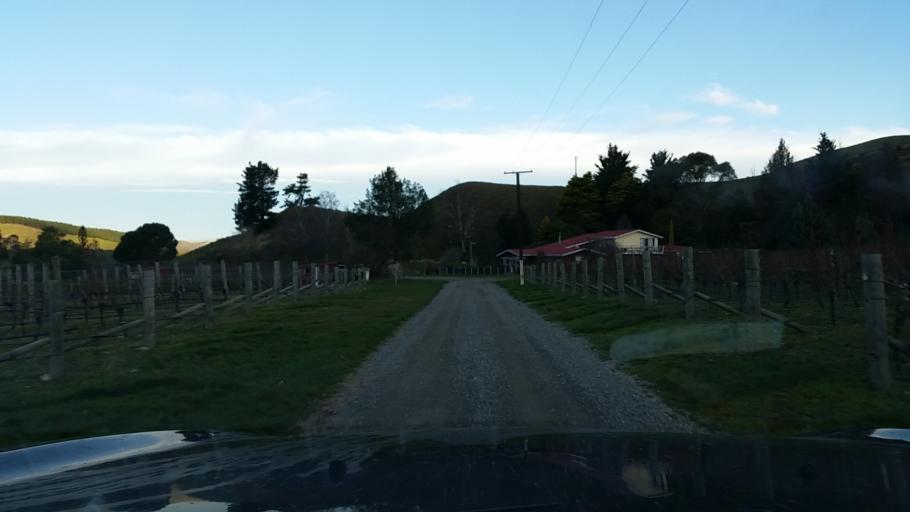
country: NZ
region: Nelson
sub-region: Nelson City
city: Nelson
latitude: -41.5055
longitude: 173.5772
